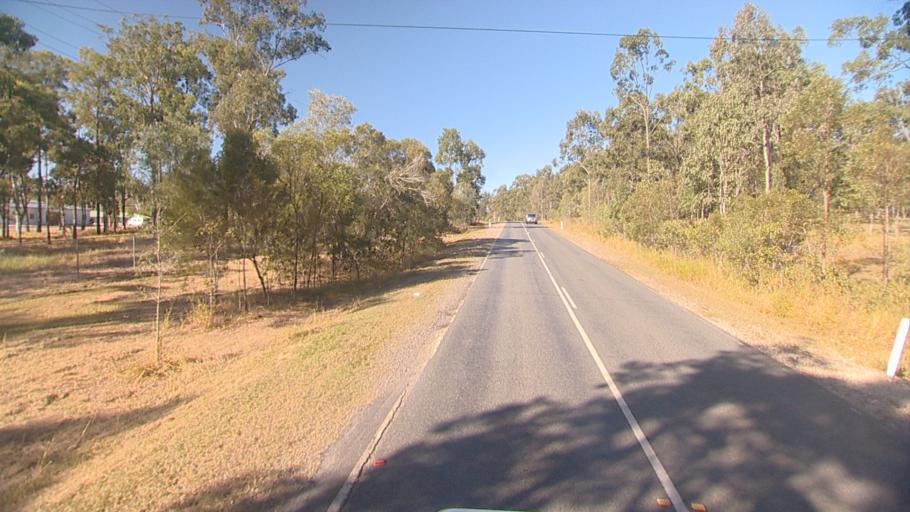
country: AU
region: Queensland
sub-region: Logan
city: North Maclean
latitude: -27.7911
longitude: 153.0358
